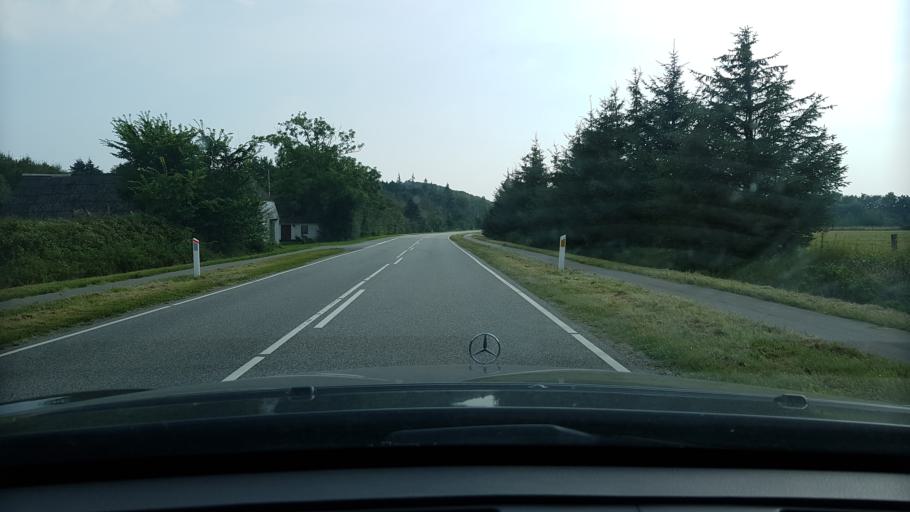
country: DK
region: North Denmark
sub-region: Alborg Kommune
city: Hals
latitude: 56.9225
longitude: 10.2613
